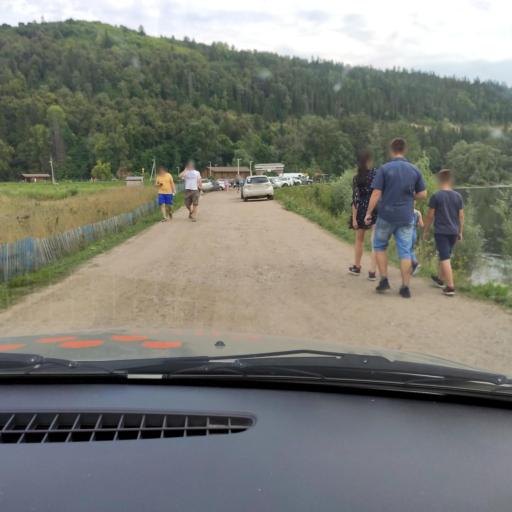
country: RU
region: Bashkortostan
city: Krasnyy Klyuch
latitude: 55.3780
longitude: 56.6759
